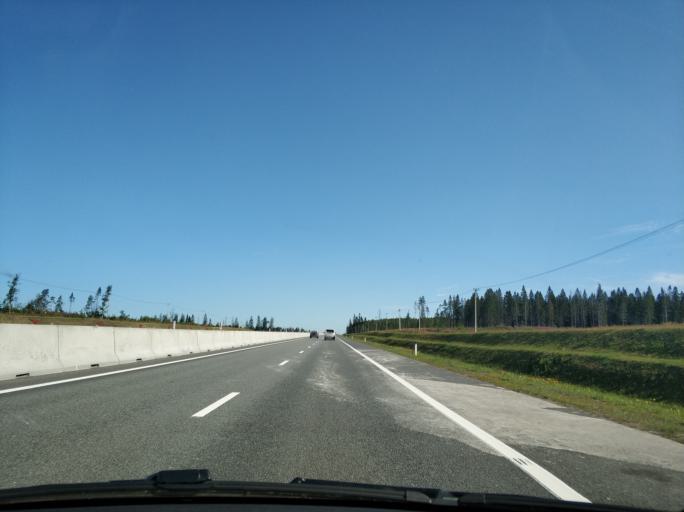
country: RU
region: Leningrad
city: Sosnovo
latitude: 60.4811
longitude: 30.1959
